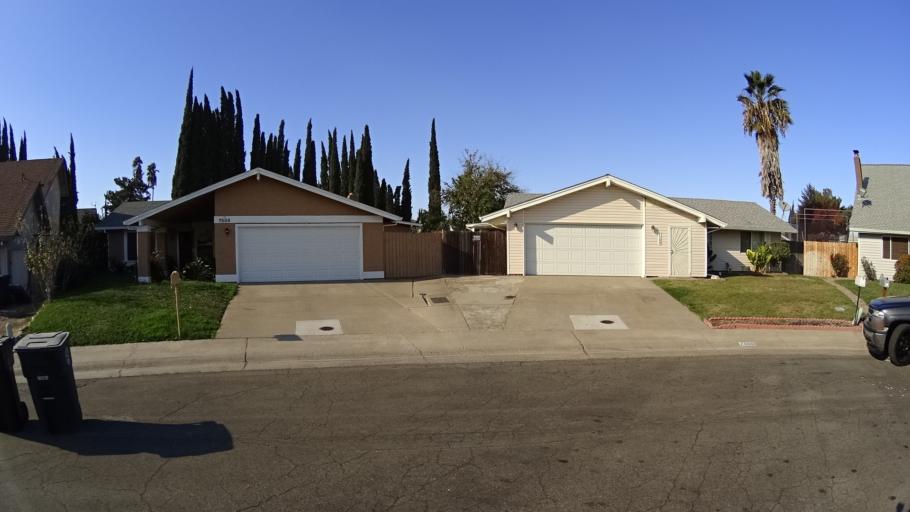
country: US
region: California
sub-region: Sacramento County
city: Antelope
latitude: 38.7019
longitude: -121.3234
